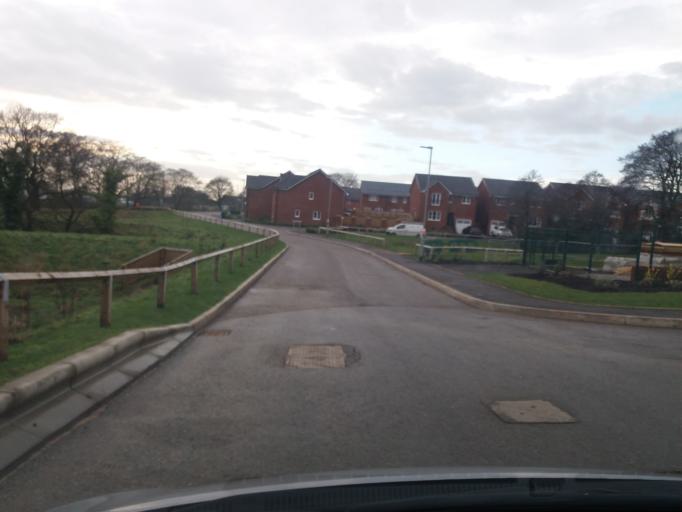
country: GB
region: England
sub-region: Lancashire
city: Adlington
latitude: 53.6123
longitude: -2.5952
